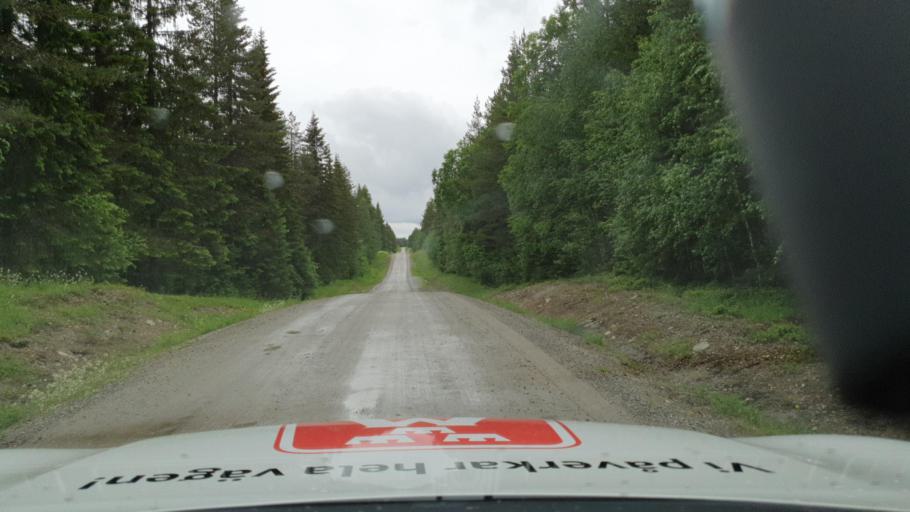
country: SE
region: Vaesterbotten
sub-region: Dorotea Kommun
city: Dorotea
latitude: 64.0626
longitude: 16.7124
